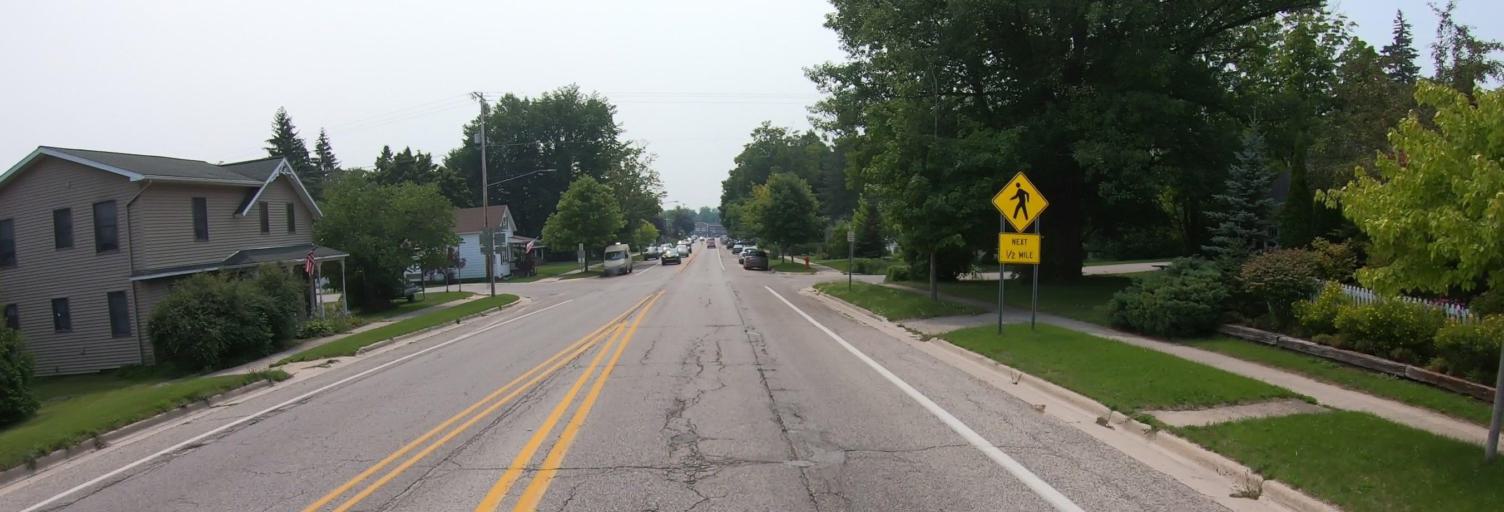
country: US
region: Michigan
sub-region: Leelanau County
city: Leland
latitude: 44.9801
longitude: -85.6477
